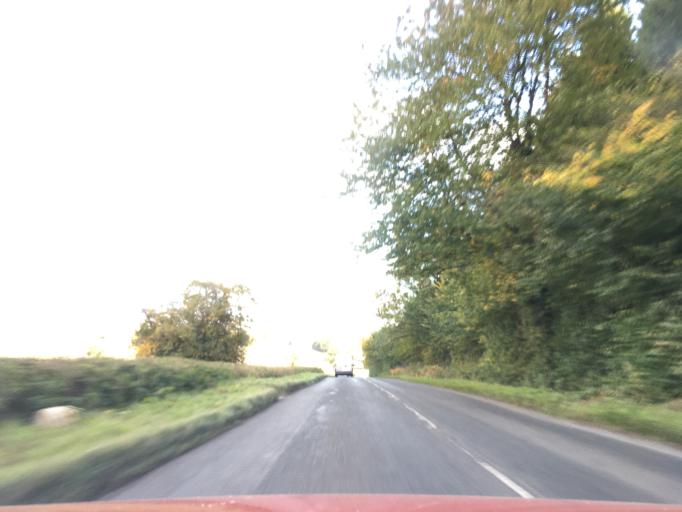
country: GB
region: England
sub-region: Herefordshire
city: Moccas
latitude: 52.1027
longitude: -2.9476
